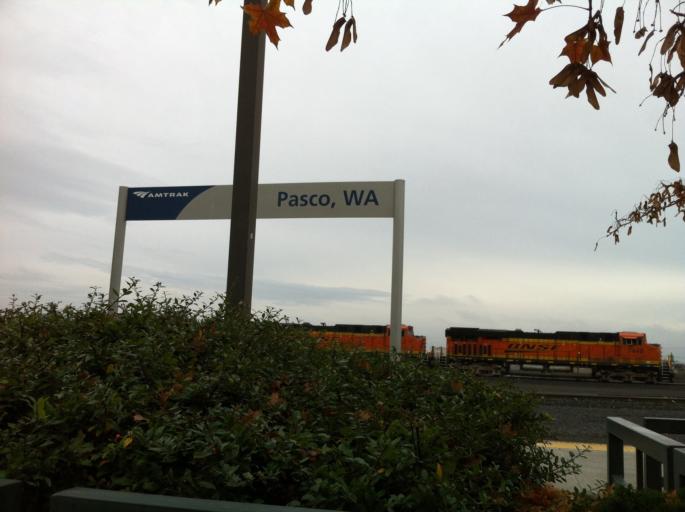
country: US
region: Washington
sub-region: Franklin County
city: Pasco
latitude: 46.2366
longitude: -119.0871
